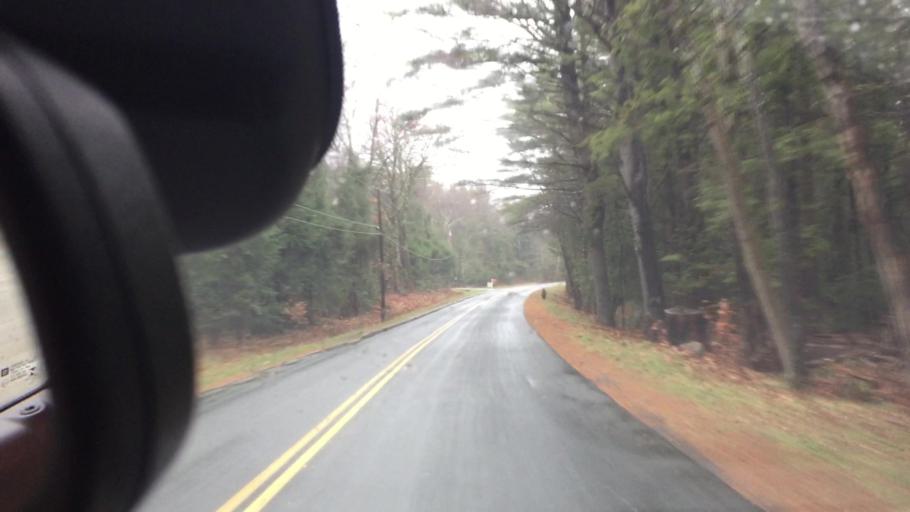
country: US
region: Massachusetts
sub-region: Berkshire County
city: Otis
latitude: 42.1896
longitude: -73.0322
